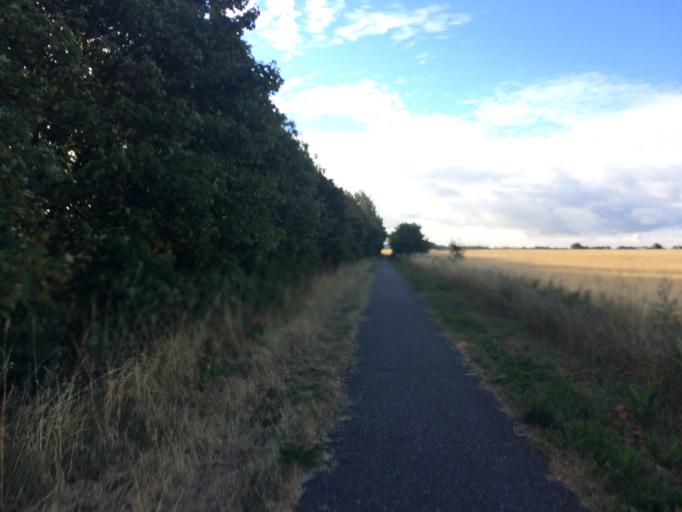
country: DK
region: Central Jutland
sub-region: Skive Kommune
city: Skive
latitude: 56.5940
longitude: 9.0059
